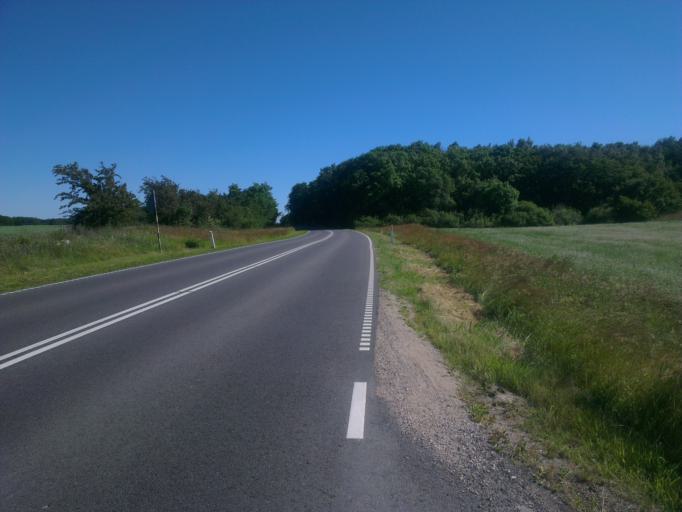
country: DK
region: Capital Region
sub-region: Frederikssund Kommune
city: Jaegerspris
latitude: 55.8784
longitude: 11.9546
